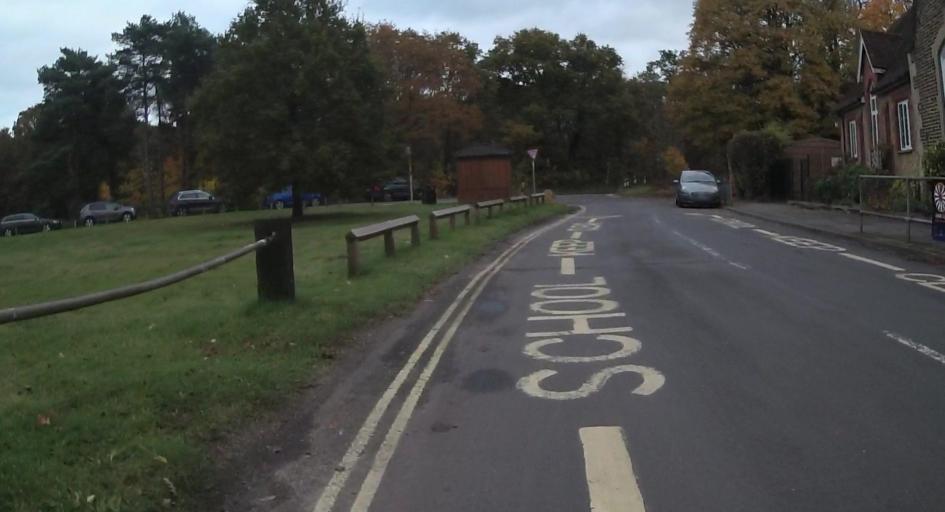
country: GB
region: England
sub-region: Surrey
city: Churt
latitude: 51.1668
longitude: -0.7889
